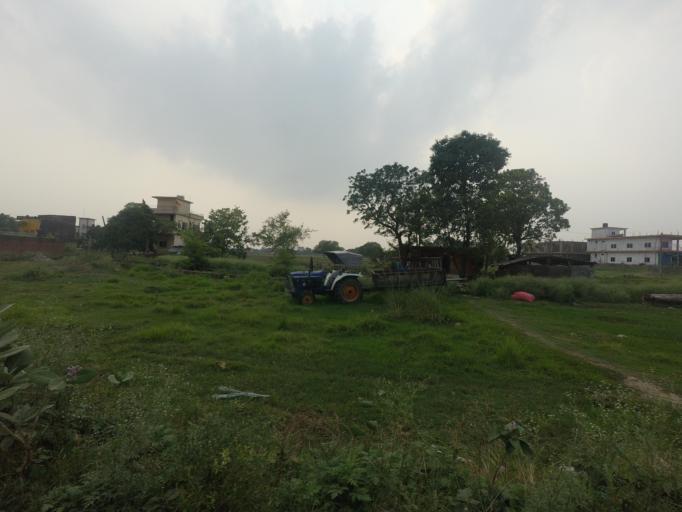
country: NP
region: Western Region
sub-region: Lumbini Zone
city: Bhairahawa
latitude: 27.5093
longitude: 83.4306
